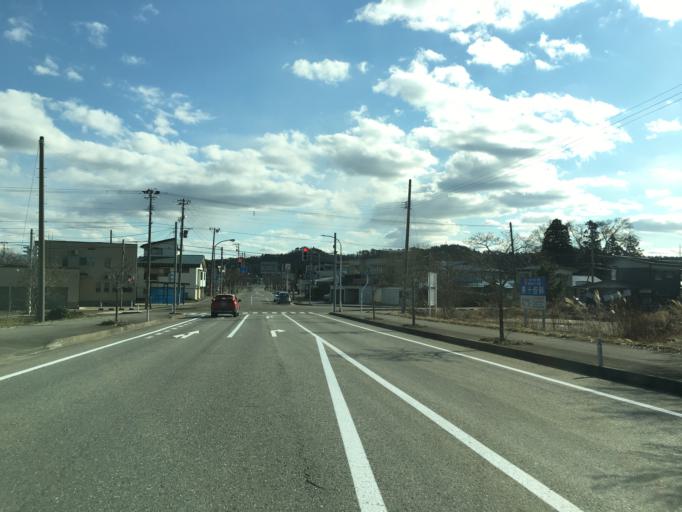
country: JP
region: Yamagata
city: Nagai
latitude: 38.0064
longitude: 140.0407
